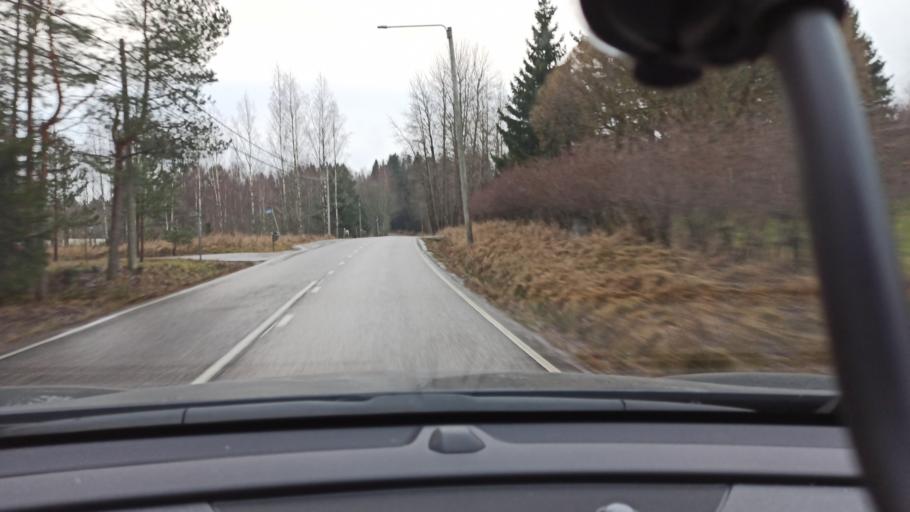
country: FI
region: Uusimaa
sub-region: Helsinki
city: Kirkkonummi
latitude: 60.1508
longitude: 24.4608
